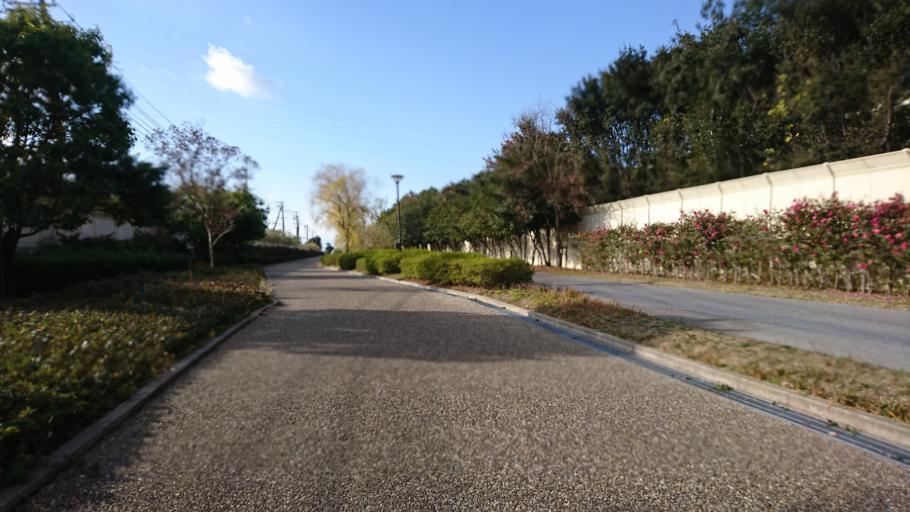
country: JP
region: Hyogo
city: Kakogawacho-honmachi
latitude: 34.7483
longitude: 134.7799
